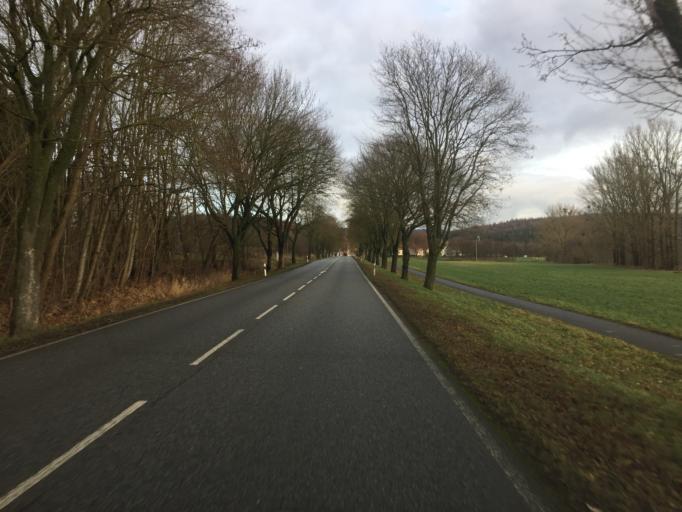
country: DE
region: Thuringia
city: Buhla
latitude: 51.4142
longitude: 10.4473
